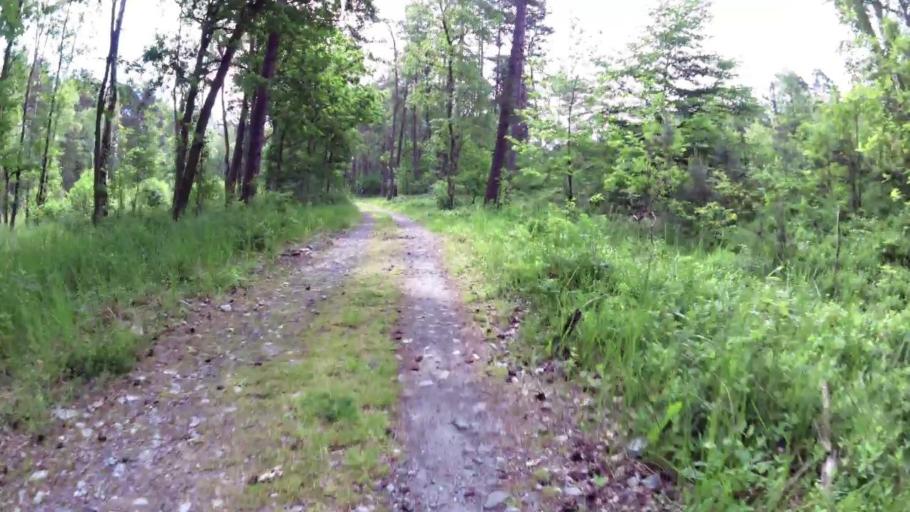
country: PL
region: West Pomeranian Voivodeship
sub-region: Swinoujscie
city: Swinoujscie
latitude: 53.9119
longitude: 14.3017
